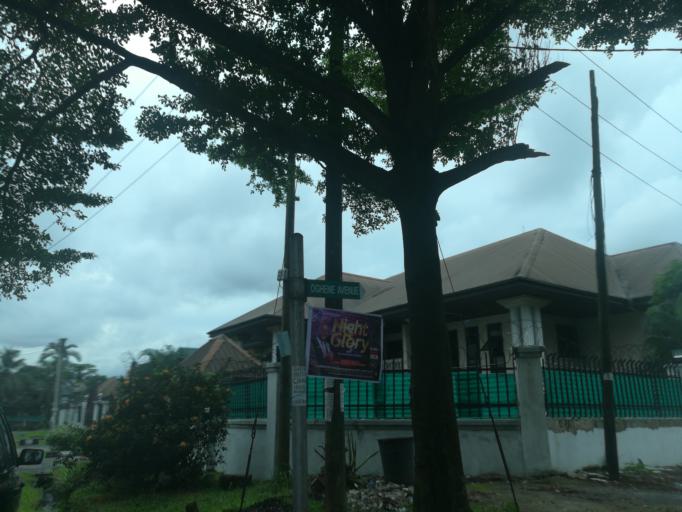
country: NG
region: Rivers
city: Port Harcourt
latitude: 4.8186
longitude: 6.9986
